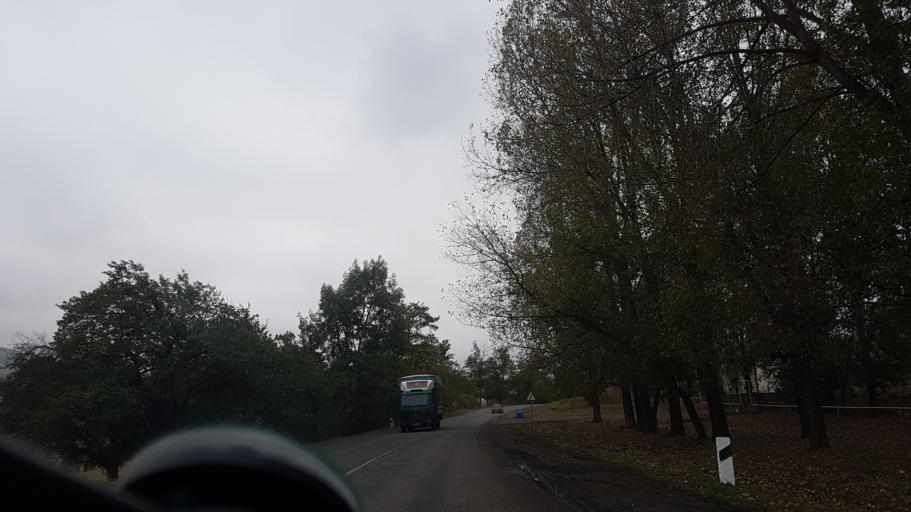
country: AZ
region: Gadabay Rayon
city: Ariqdam
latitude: 40.6469
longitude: 45.8119
